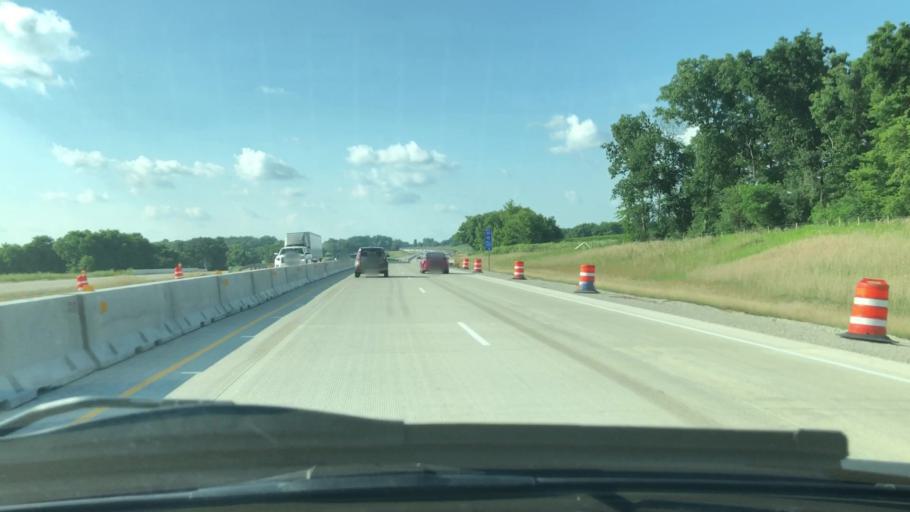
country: US
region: Wisconsin
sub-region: Jefferson County
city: Cambridge
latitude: 42.9509
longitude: -89.0955
